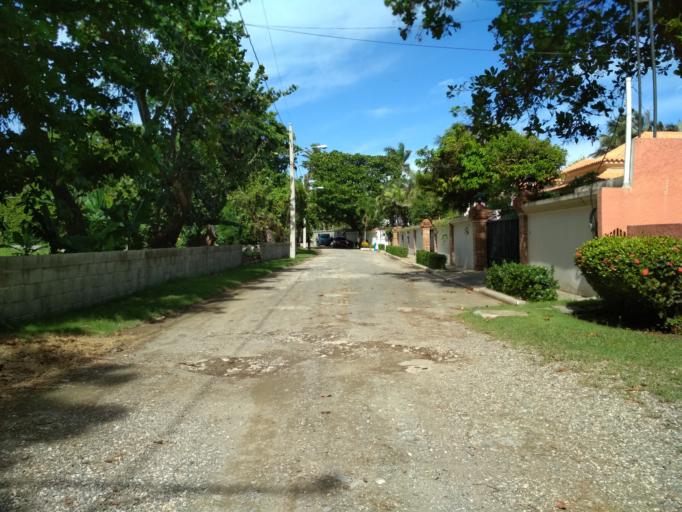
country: DO
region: Puerto Plata
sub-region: Puerto Plata
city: Puerto Plata
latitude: 19.8082
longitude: -70.7062
